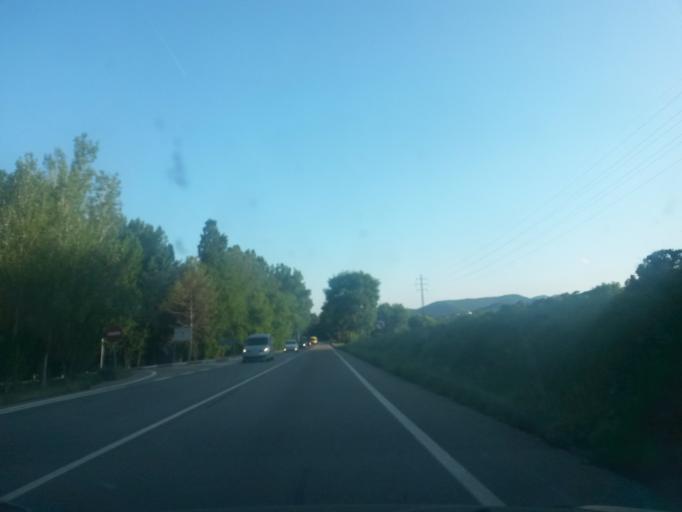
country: ES
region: Catalonia
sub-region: Provincia de Girona
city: Porqueres
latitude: 42.1617
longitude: 2.7457
